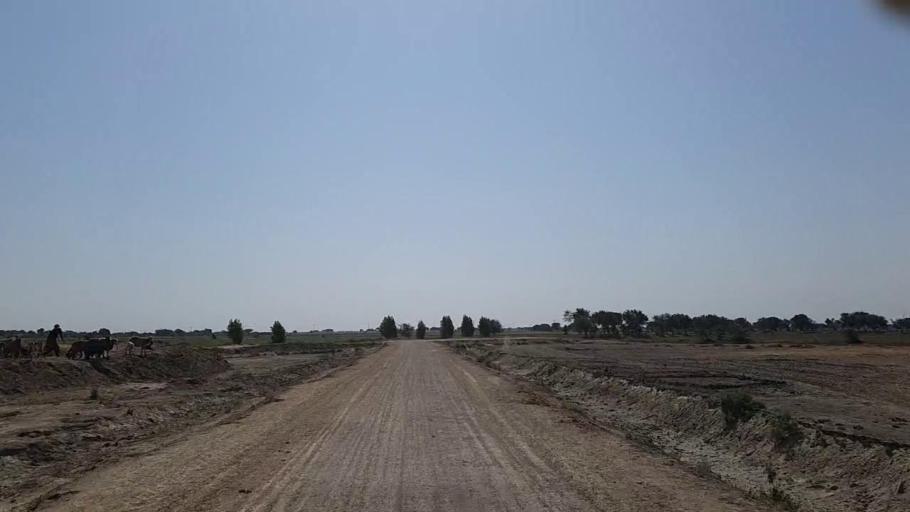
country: PK
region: Sindh
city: Mirpur Batoro
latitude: 24.6824
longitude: 68.2880
